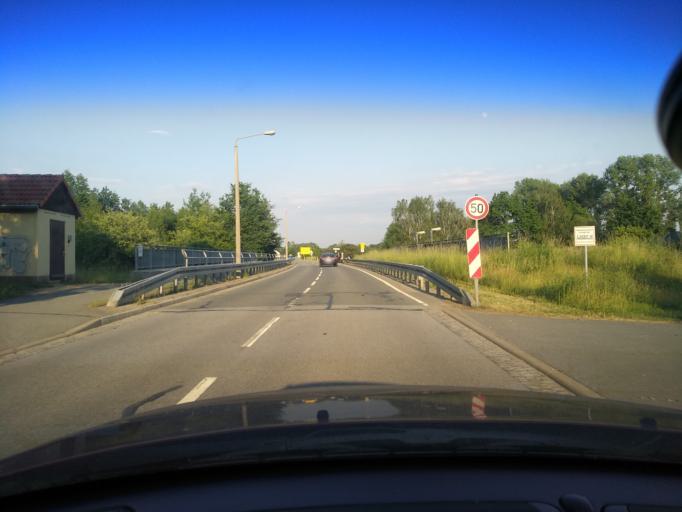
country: DE
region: Saxony
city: Ostritz
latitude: 51.0673
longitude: 14.9506
